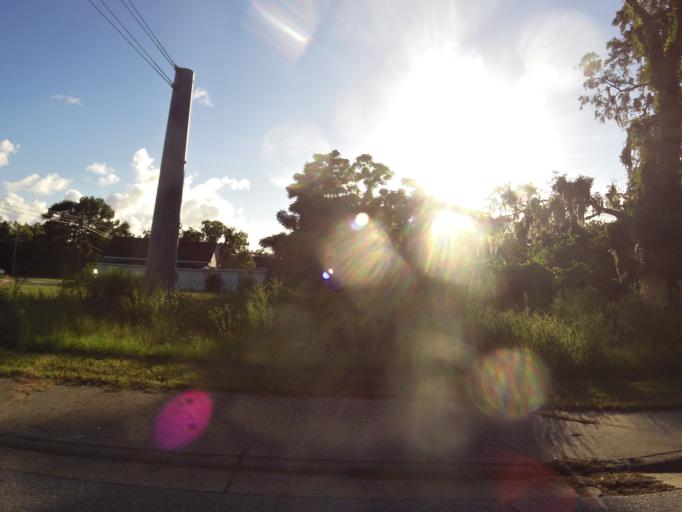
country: US
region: Georgia
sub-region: Glynn County
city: Brunswick
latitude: 31.1606
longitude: -81.4916
